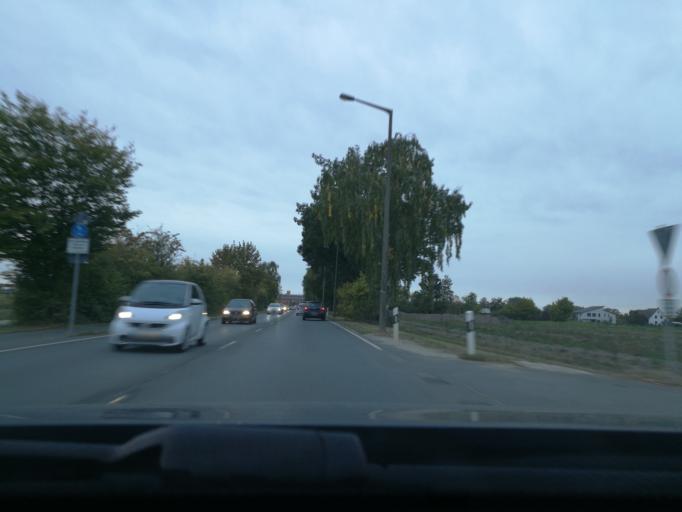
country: DE
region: Bavaria
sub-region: Regierungsbezirk Mittelfranken
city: Wetzendorf
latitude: 49.4846
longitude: 11.0646
